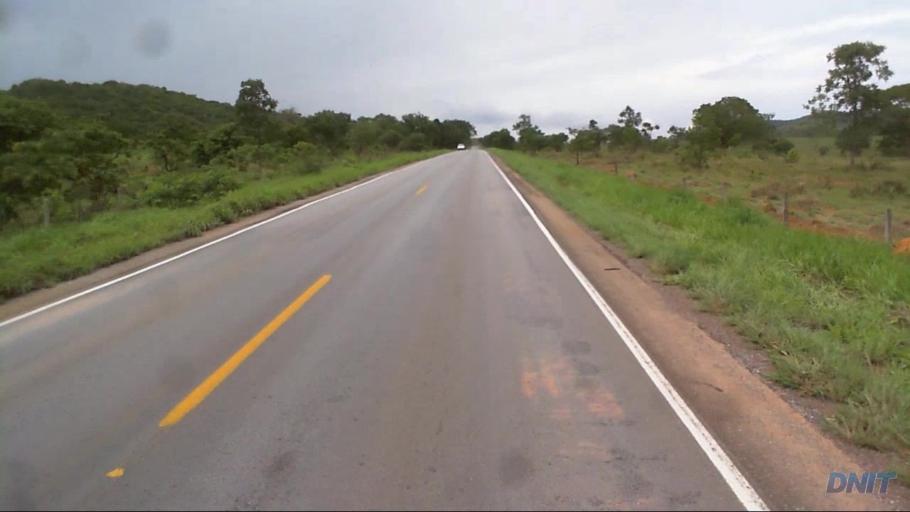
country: BR
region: Goias
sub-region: Padre Bernardo
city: Padre Bernardo
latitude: -15.4502
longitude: -48.2075
